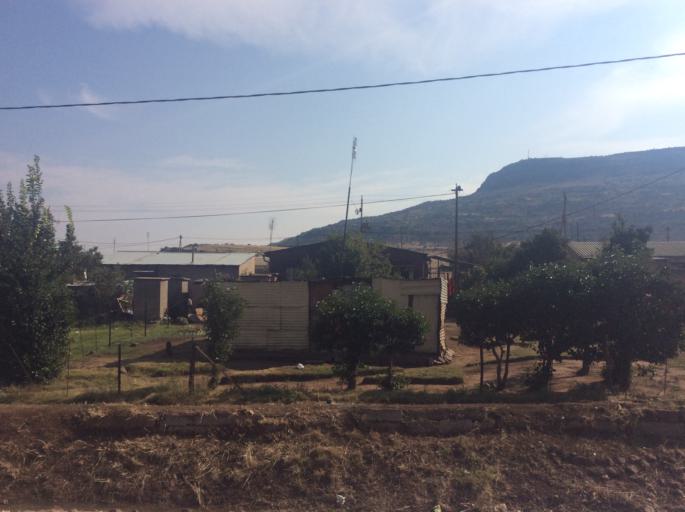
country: LS
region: Mafeteng
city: Mafeteng
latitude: -29.7190
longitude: 27.0282
